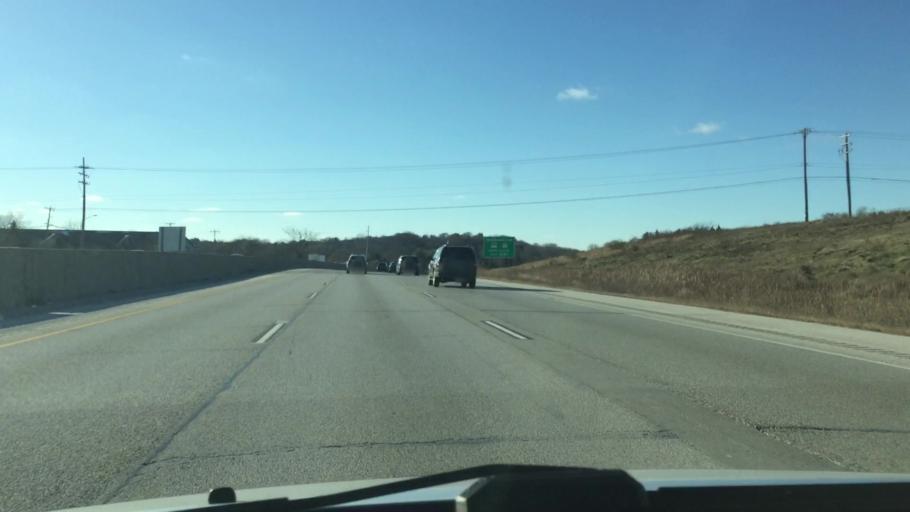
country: US
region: Wisconsin
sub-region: Waukesha County
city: Pewaukee
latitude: 43.0461
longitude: -88.2642
